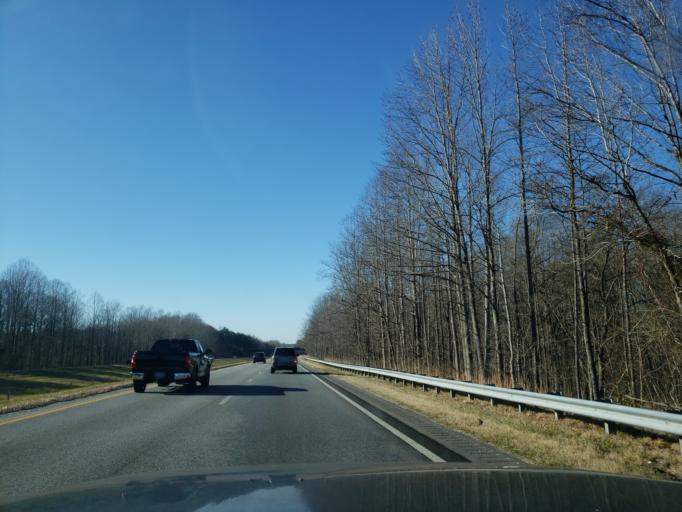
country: US
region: North Carolina
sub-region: Davidson County
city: Wallburg
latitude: 36.0294
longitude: -80.0675
